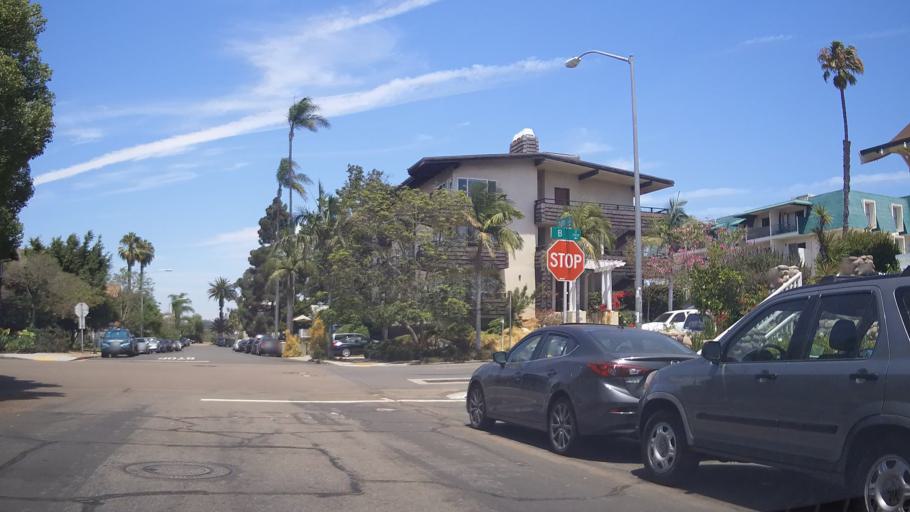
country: US
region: California
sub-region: San Diego County
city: San Diego
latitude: 32.7176
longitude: -117.1425
